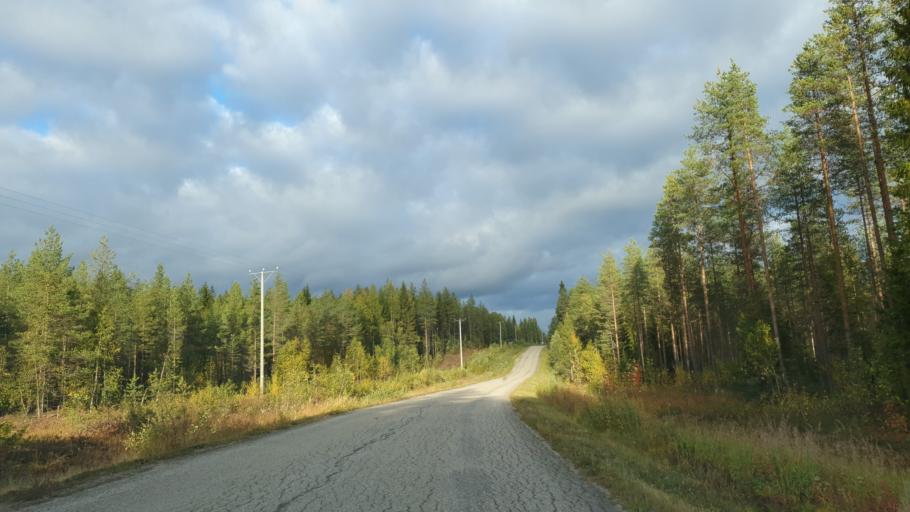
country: FI
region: North Karelia
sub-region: Pielisen Karjala
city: Lieksa
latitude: 63.9202
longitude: 30.1339
